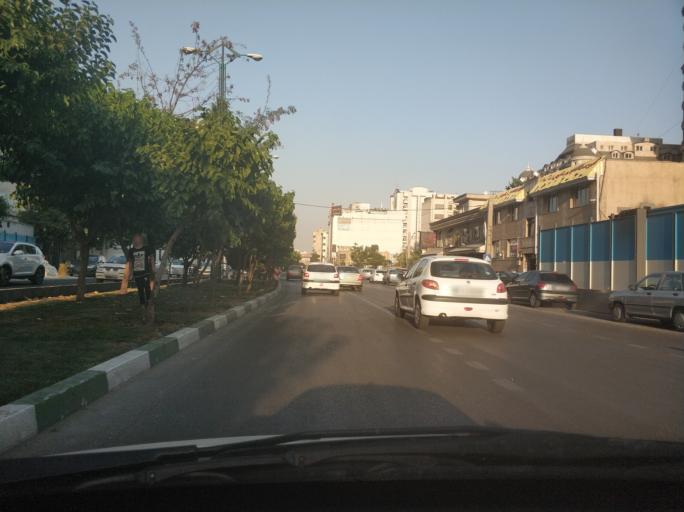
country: IR
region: Tehran
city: Tajrish
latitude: 35.7996
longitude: 51.4704
